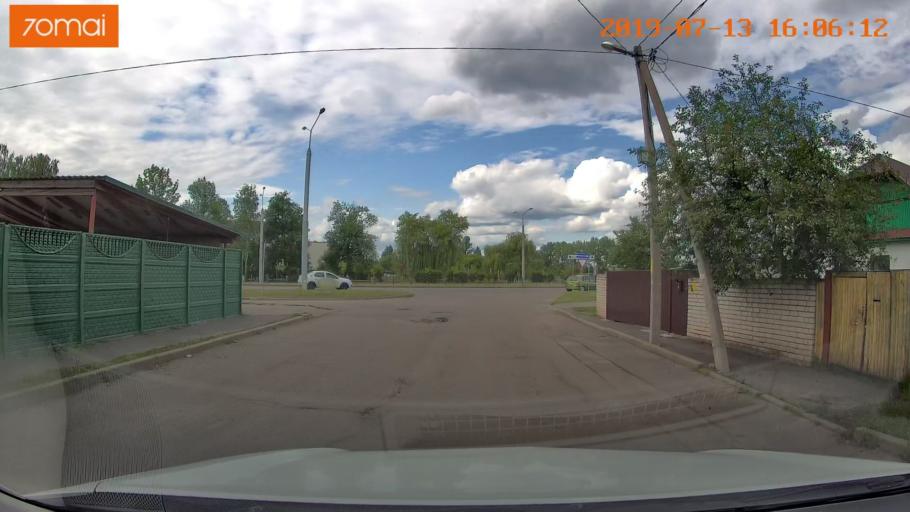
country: BY
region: Mogilev
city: Babruysk
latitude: 53.1524
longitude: 29.2047
